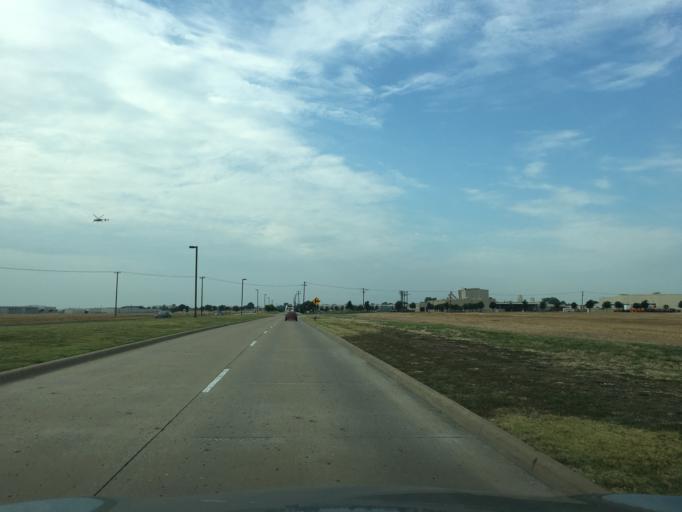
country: US
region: Texas
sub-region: Collin County
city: McKinney
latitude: 33.1871
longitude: -96.5981
